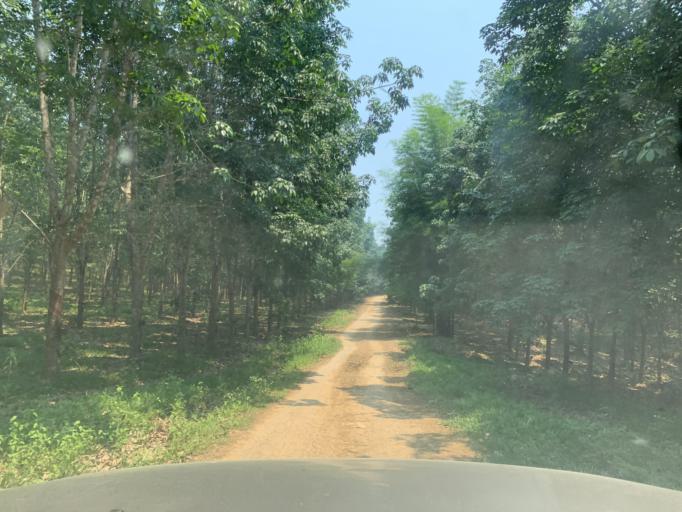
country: LA
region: Louangphabang
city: Xiang Ngeun
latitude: 19.8292
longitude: 102.2191
